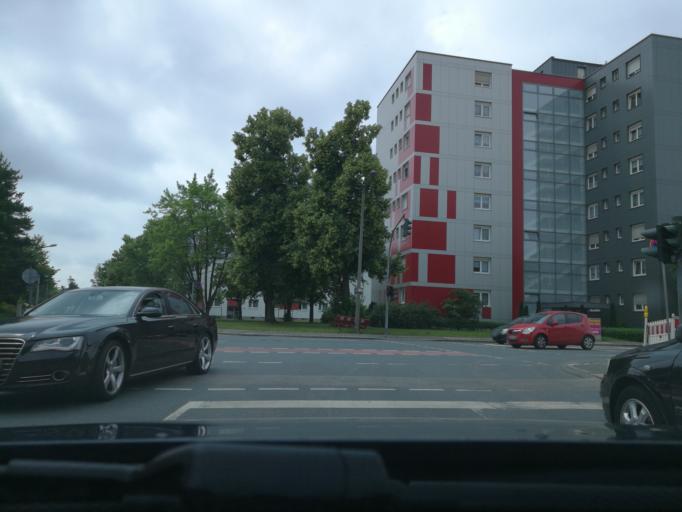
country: DE
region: Bavaria
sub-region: Regierungsbezirk Mittelfranken
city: Furth
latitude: 49.4783
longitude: 10.9702
